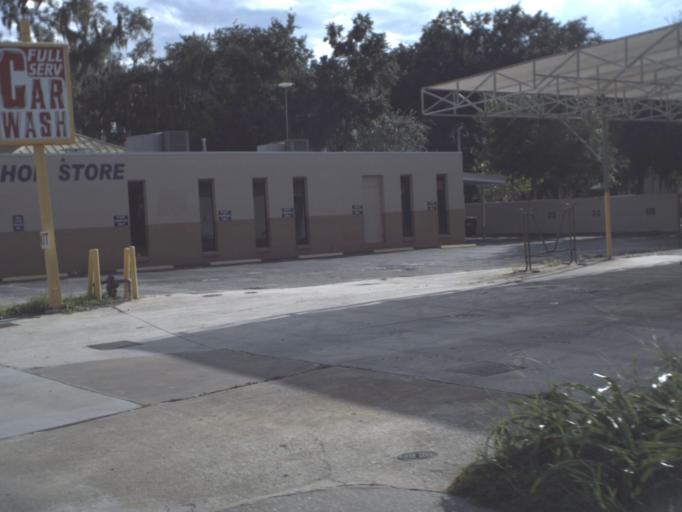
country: US
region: Florida
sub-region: Polk County
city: Winter Haven
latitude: 28.0238
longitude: -81.7330
